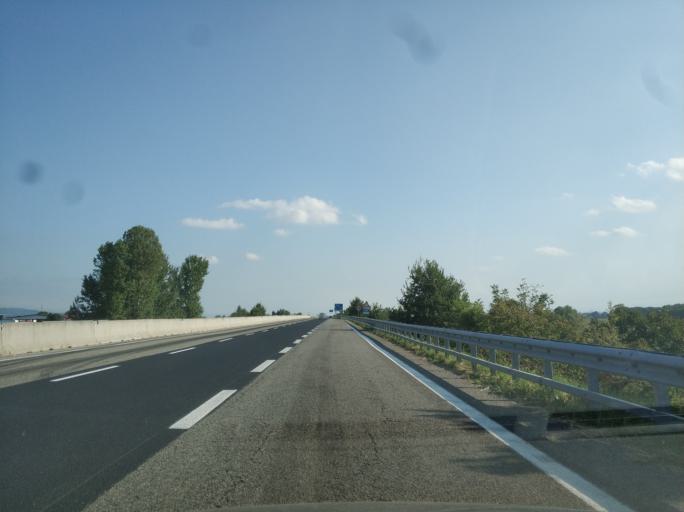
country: IT
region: Piedmont
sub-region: Provincia di Cuneo
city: Bra
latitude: 44.6969
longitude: 7.8246
